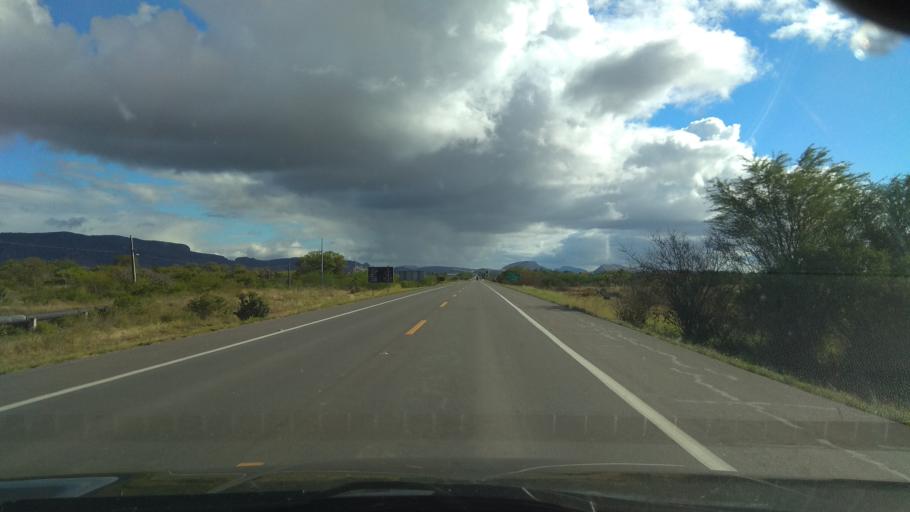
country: BR
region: Bahia
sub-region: Castro Alves
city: Castro Alves
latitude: -12.6904
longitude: -39.6916
